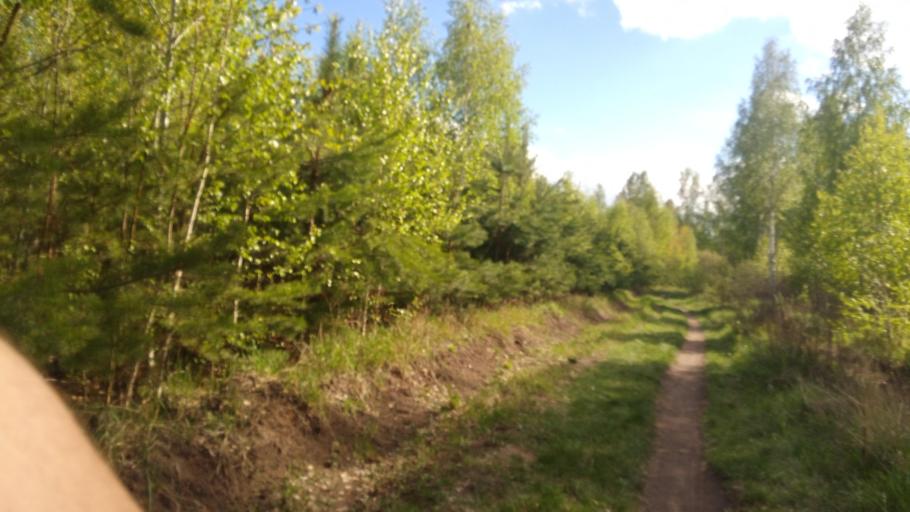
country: RU
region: Chelyabinsk
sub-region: Gorod Chelyabinsk
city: Chelyabinsk
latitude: 55.1662
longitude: 61.3169
